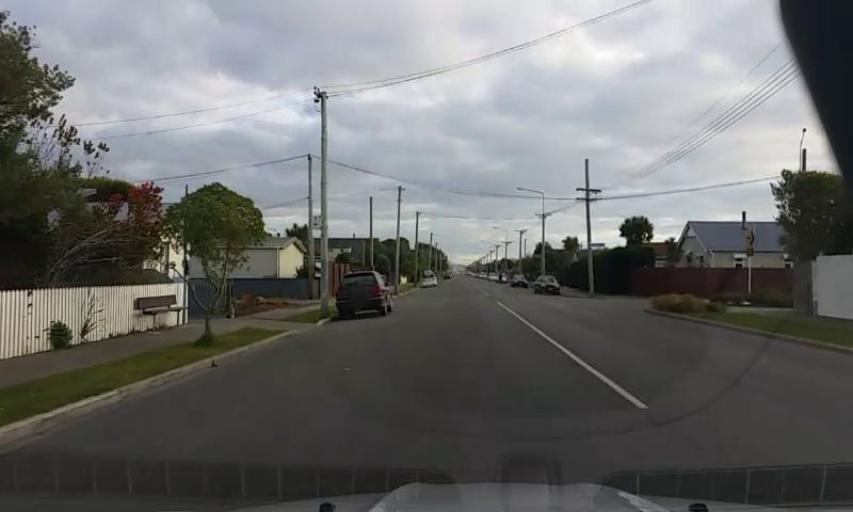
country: NZ
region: Canterbury
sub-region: Christchurch City
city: Christchurch
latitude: -43.5305
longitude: 172.7358
